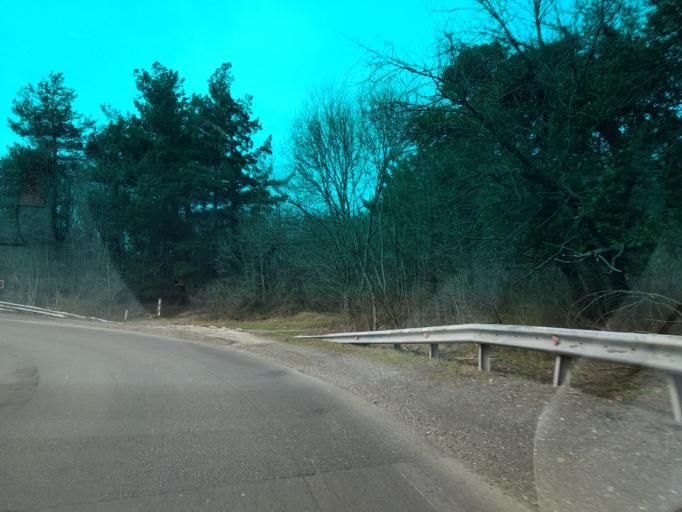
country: RU
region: Krasnodarskiy
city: Shepsi
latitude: 44.0447
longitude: 39.1425
